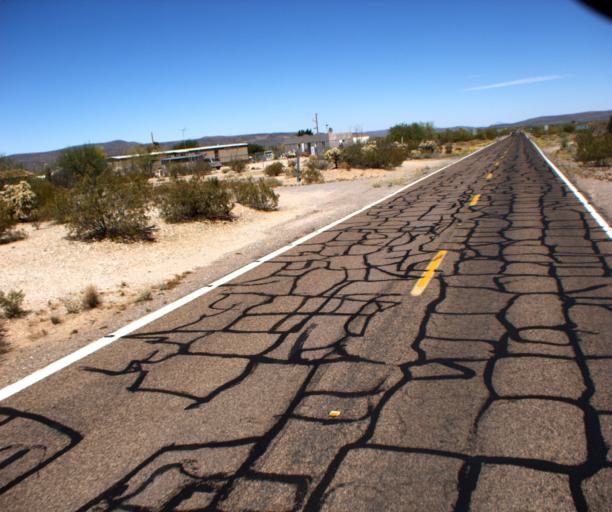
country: US
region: Arizona
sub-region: Pima County
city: Ajo
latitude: 32.4095
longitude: -112.8718
